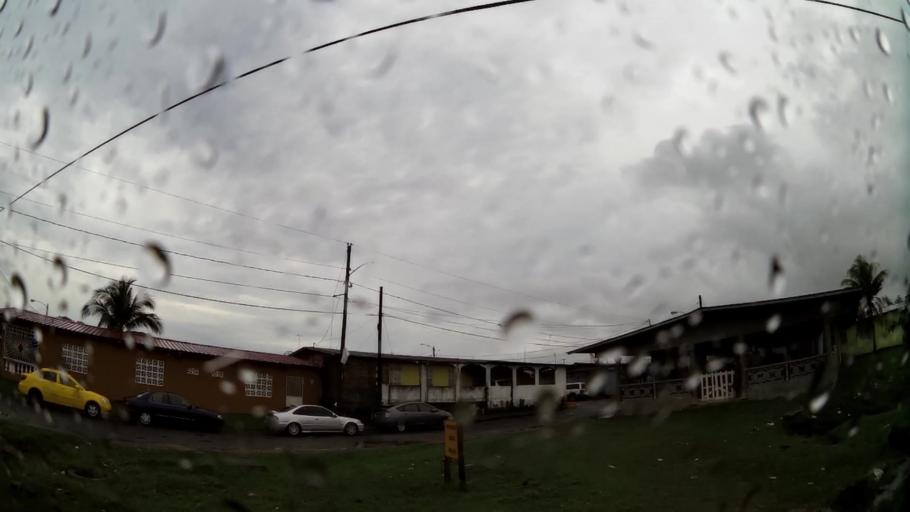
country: PA
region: Colon
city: Las Margaritas
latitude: 9.3320
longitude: -79.8737
